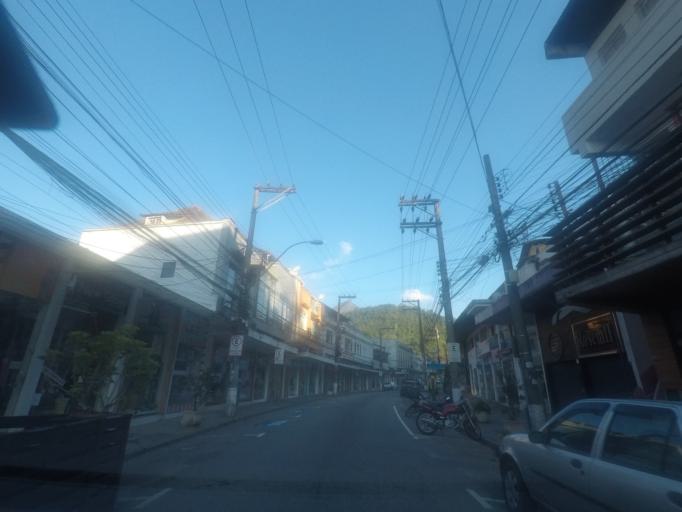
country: BR
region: Rio de Janeiro
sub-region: Petropolis
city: Petropolis
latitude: -22.5154
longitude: -43.1723
